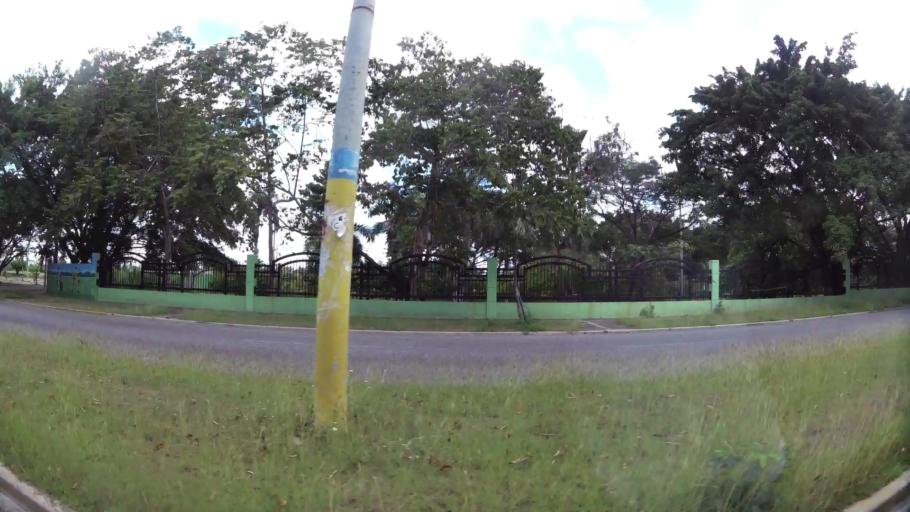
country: DO
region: Santo Domingo
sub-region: Santo Domingo
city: Santo Domingo Este
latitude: 18.4778
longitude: -69.8637
